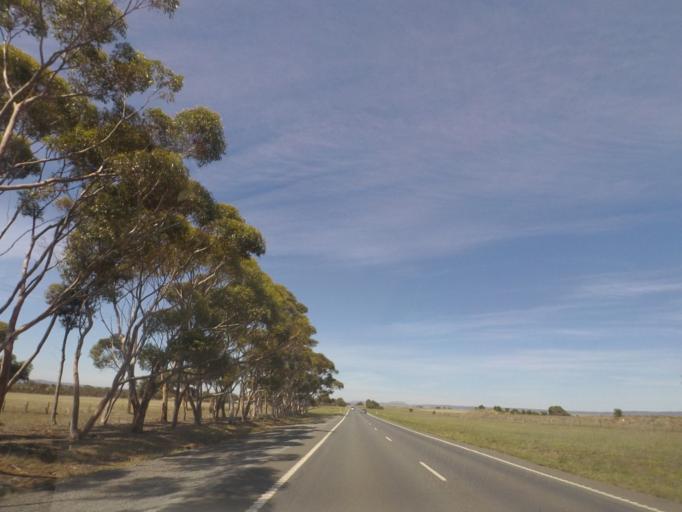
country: AU
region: Victoria
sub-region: Moorabool
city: Bacchus Marsh
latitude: -37.7836
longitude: 144.4279
